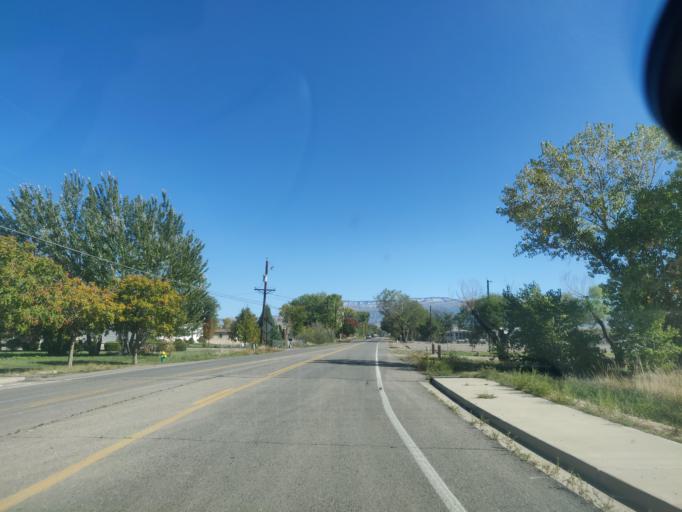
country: US
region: Colorado
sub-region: Mesa County
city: Fruitvale
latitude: 39.0700
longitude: -108.5114
